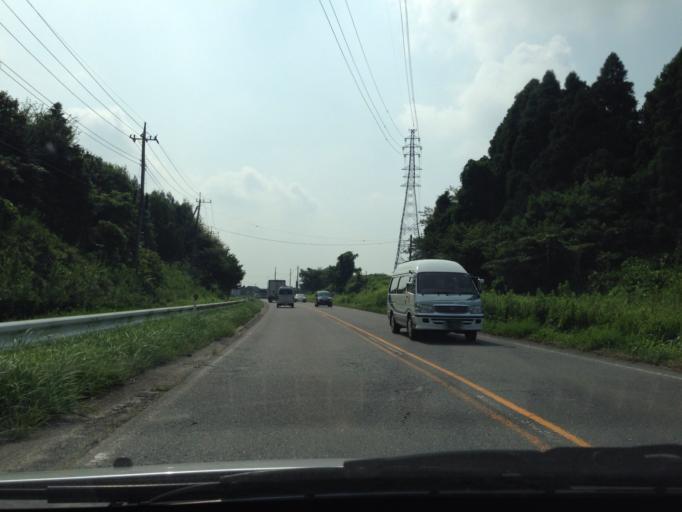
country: JP
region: Ibaraki
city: Ami
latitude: 36.0235
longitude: 140.2387
